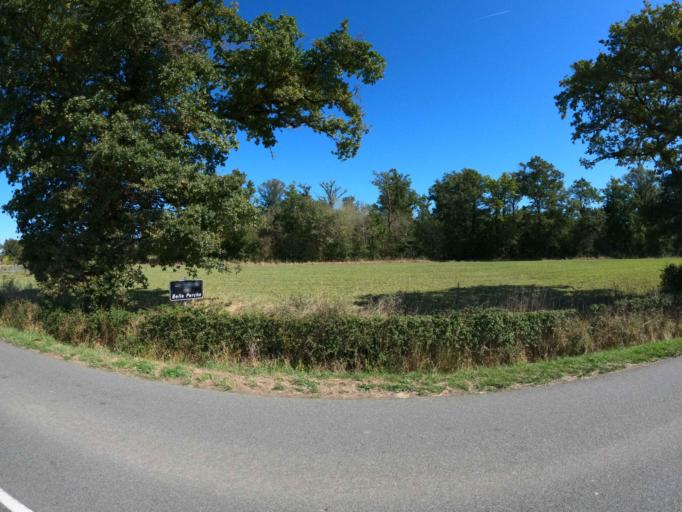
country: FR
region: Poitou-Charentes
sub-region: Departement de la Vienne
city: Lathus-Saint-Remy
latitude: 46.2761
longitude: 1.0180
